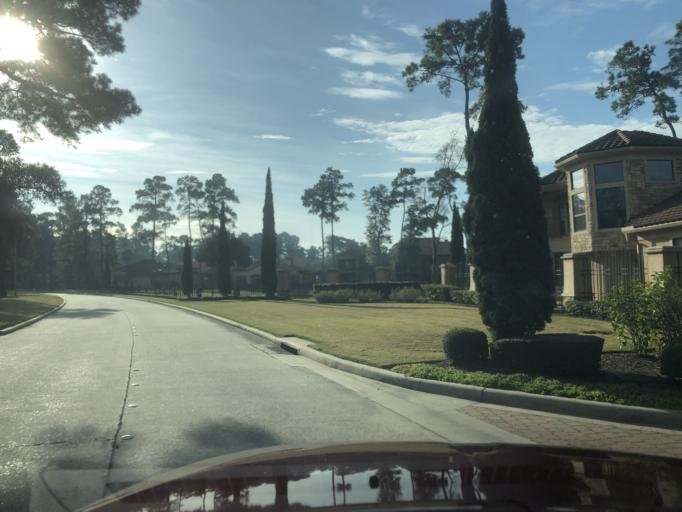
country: US
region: Texas
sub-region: Harris County
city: Spring
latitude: 30.0060
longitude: -95.4782
